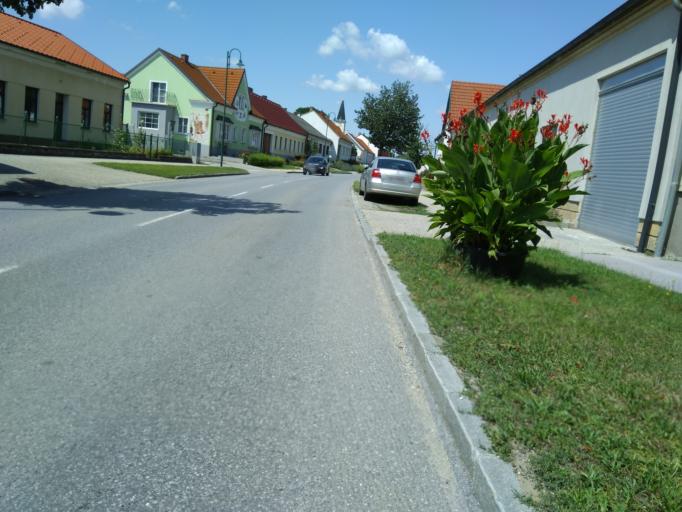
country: AT
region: Lower Austria
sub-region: Politischer Bezirk Ganserndorf
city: Ganserndorf
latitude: 48.3710
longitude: 16.6883
